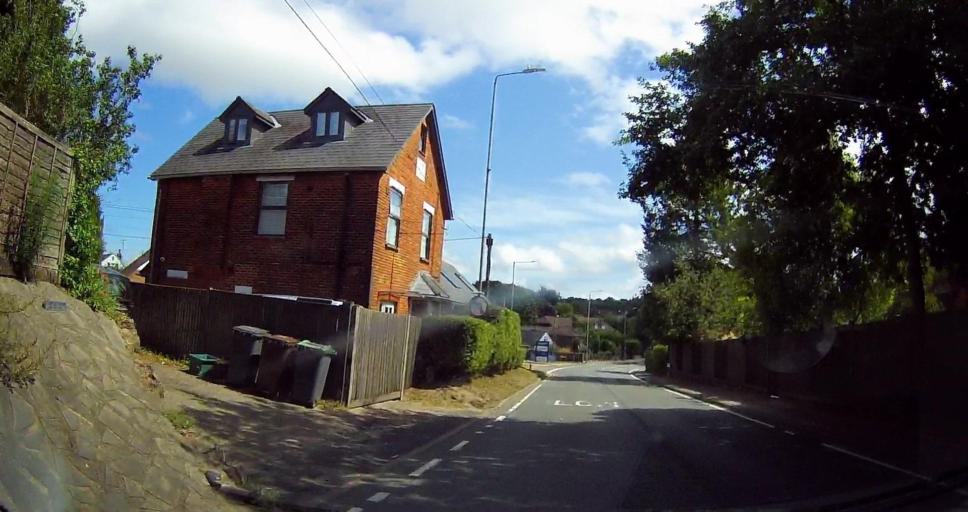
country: GB
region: England
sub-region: Kent
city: Borough Green
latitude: 51.2904
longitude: 0.3068
